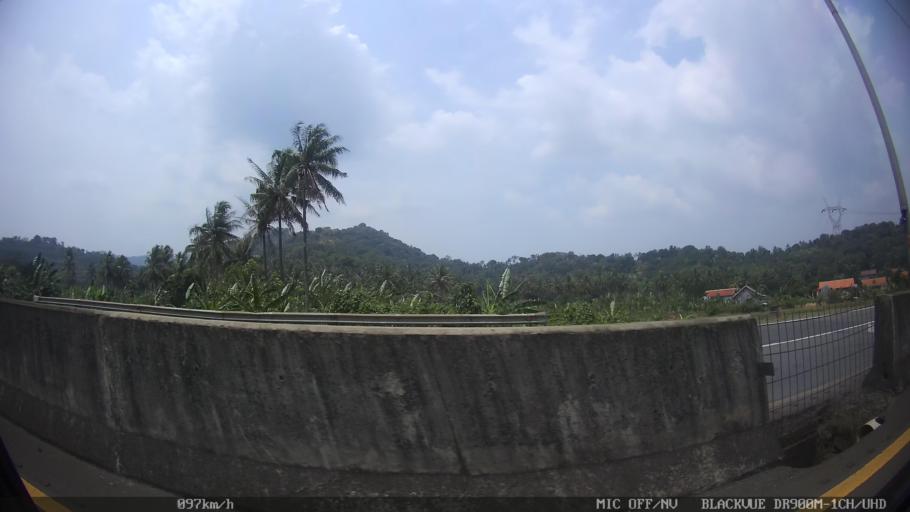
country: ID
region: Banten
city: Curug
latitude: -5.9796
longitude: 106.0194
